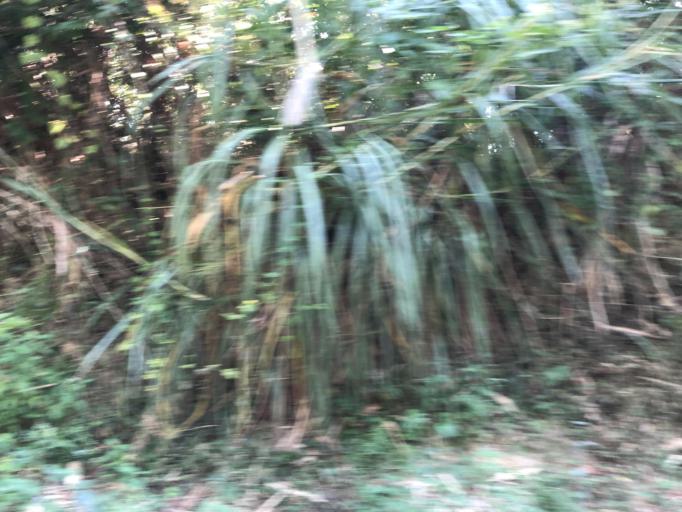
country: TW
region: Taiwan
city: Yujing
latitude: 23.0492
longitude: 120.3801
